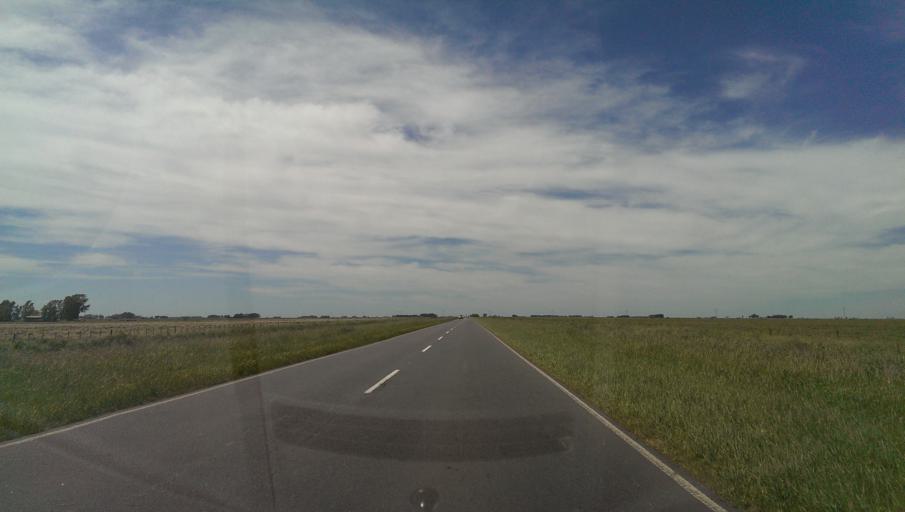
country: AR
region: Buenos Aires
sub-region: Partido de Laprida
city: Laprida
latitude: -37.2405
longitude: -60.7648
